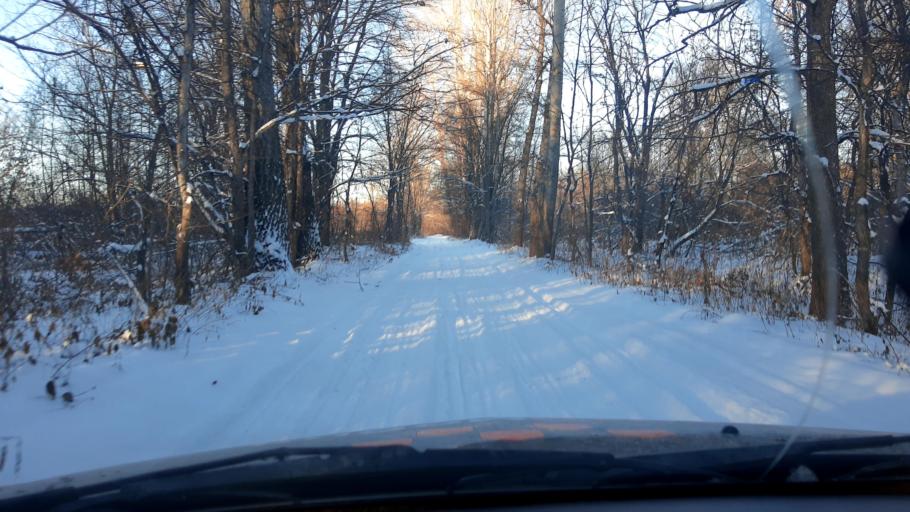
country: RU
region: Bashkortostan
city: Ufa
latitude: 54.6561
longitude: 55.9715
